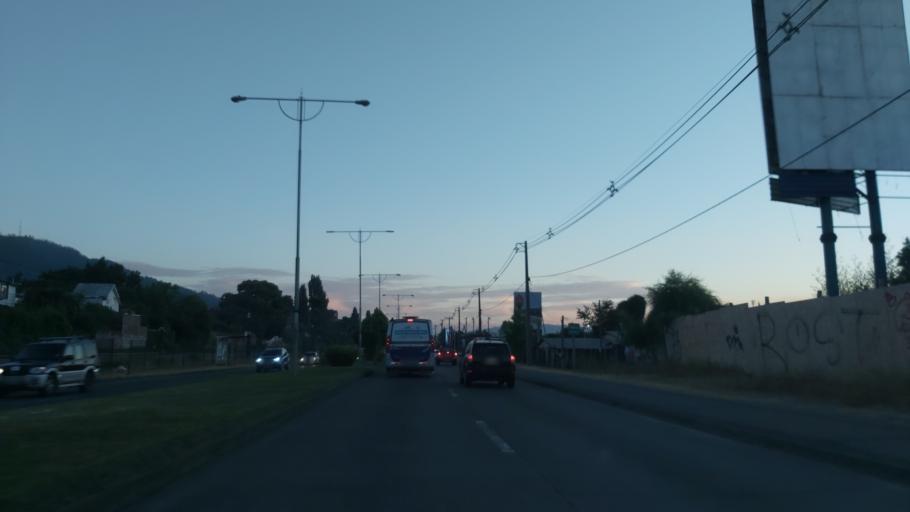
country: CL
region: Biobio
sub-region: Provincia de Concepcion
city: Chiguayante
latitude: -36.8976
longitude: -73.0328
